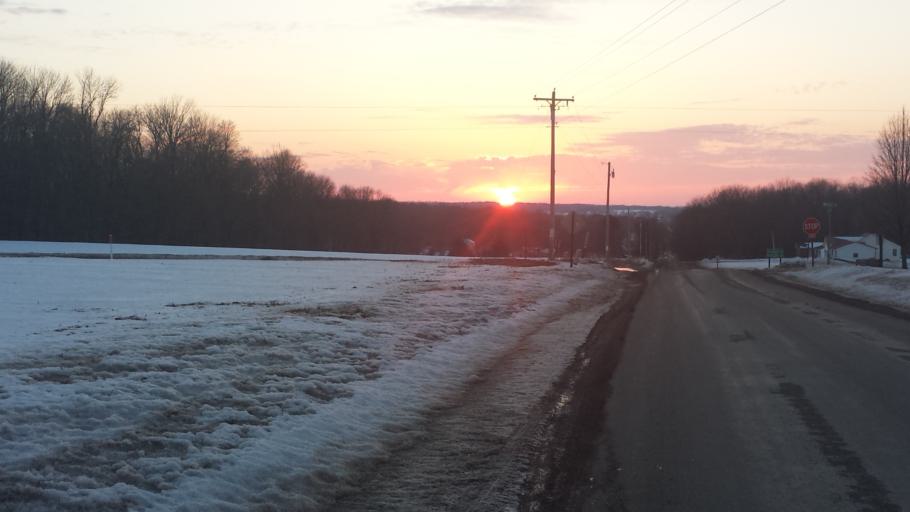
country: US
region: Ohio
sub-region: Richland County
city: Lexington
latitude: 40.6013
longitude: -82.6239
